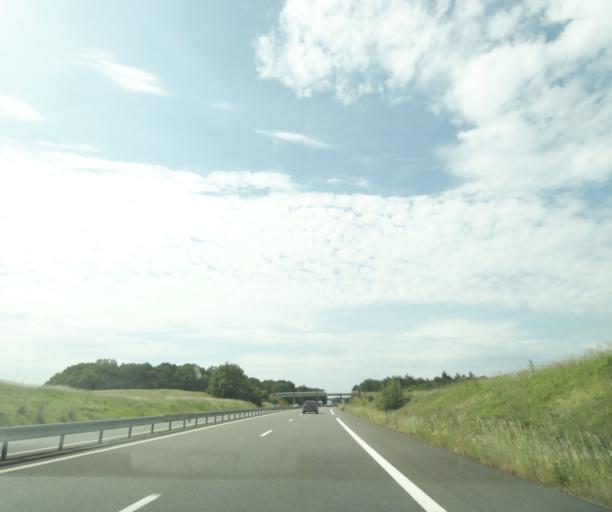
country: FR
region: Pays de la Loire
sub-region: Departement de Maine-et-Loire
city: Baune
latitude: 47.5053
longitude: -0.2881
